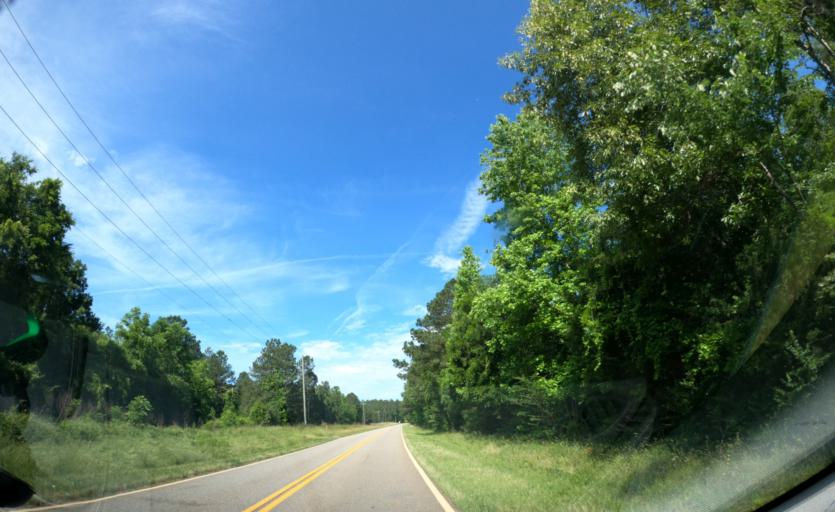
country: US
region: Georgia
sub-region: Elbert County
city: Elberton
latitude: 34.1421
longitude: -82.8050
